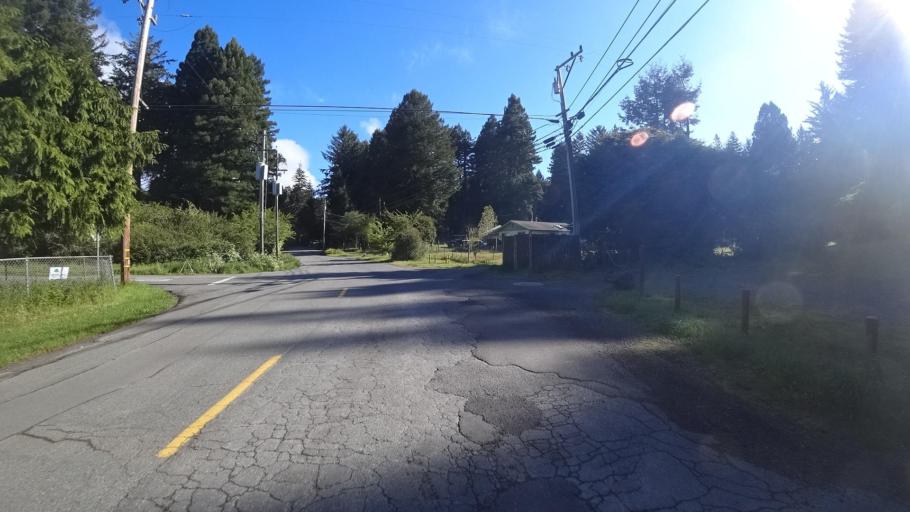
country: US
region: California
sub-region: Humboldt County
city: Westhaven-Moonstone
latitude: 41.0355
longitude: -124.1076
